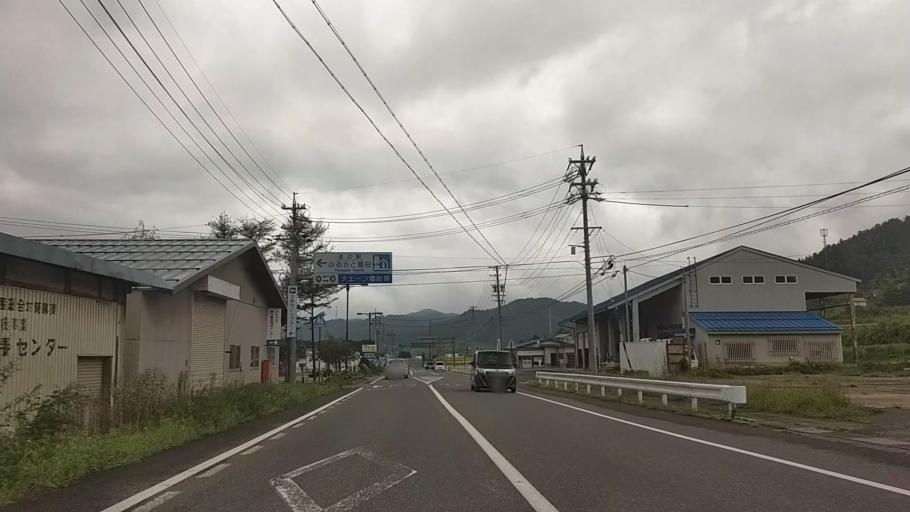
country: JP
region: Nagano
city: Iiyama
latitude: 36.8016
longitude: 138.3237
